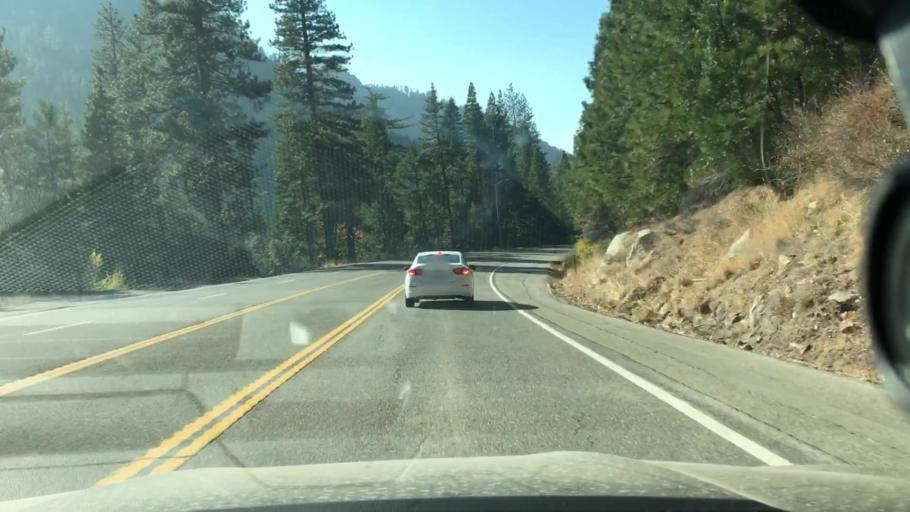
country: US
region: California
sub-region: El Dorado County
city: South Lake Tahoe
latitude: 38.7809
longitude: -120.2422
